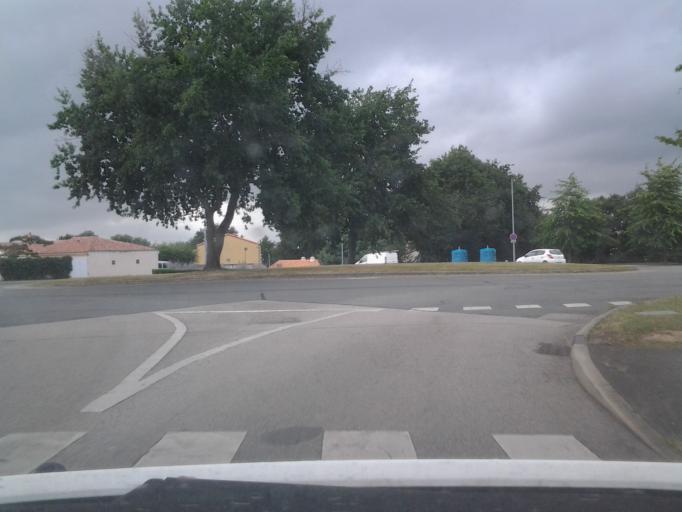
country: FR
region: Pays de la Loire
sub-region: Departement de la Vendee
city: La Roche-sur-Yon
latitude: 46.6481
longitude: -1.4392
